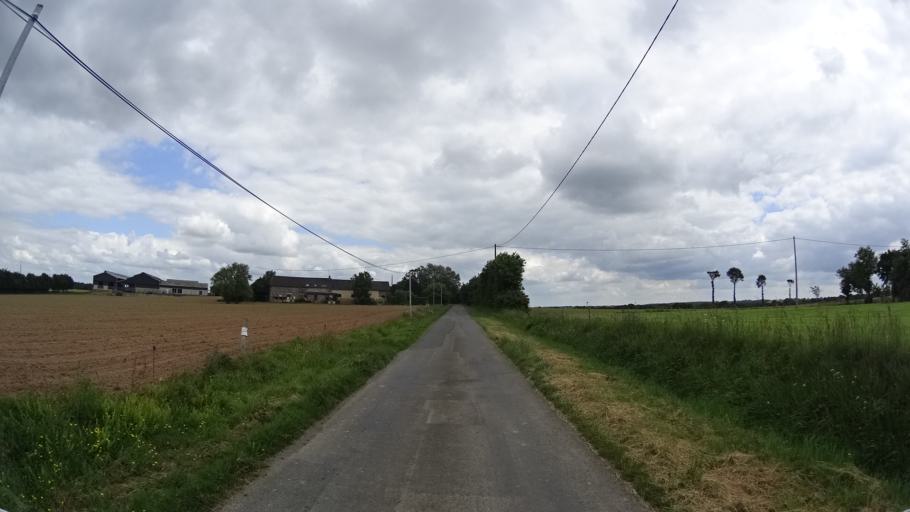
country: FR
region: Brittany
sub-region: Departement d'Ille-et-Vilaine
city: Monterfil
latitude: 48.0660
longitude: -2.0143
